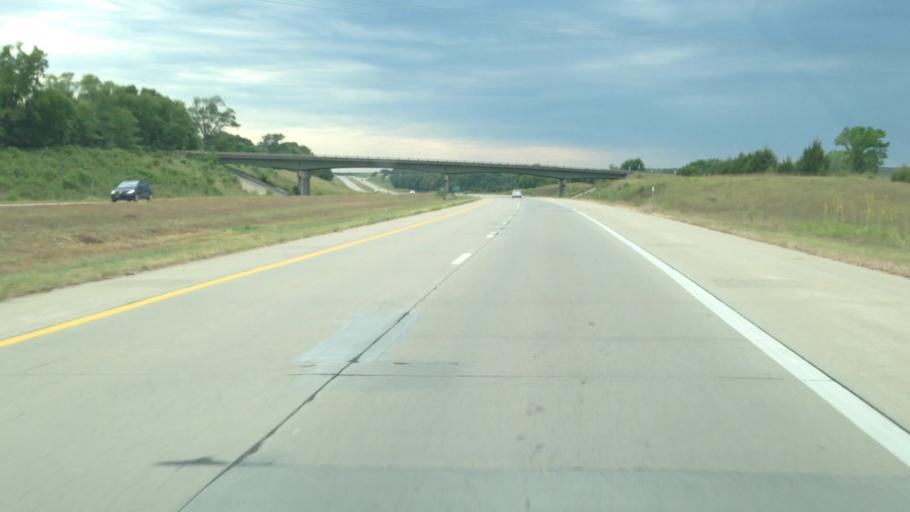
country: US
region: Kansas
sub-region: Franklin County
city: Ottawa
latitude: 38.5508
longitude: -95.3589
